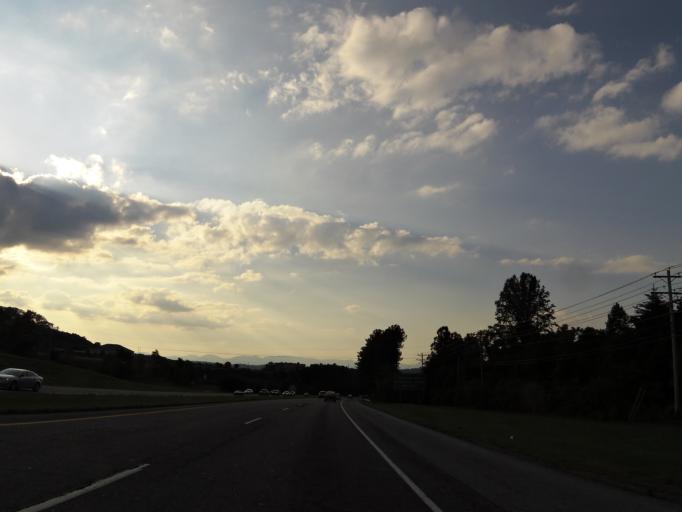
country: US
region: Tennessee
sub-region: Knox County
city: Farragut
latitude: 35.9415
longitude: -84.1523
